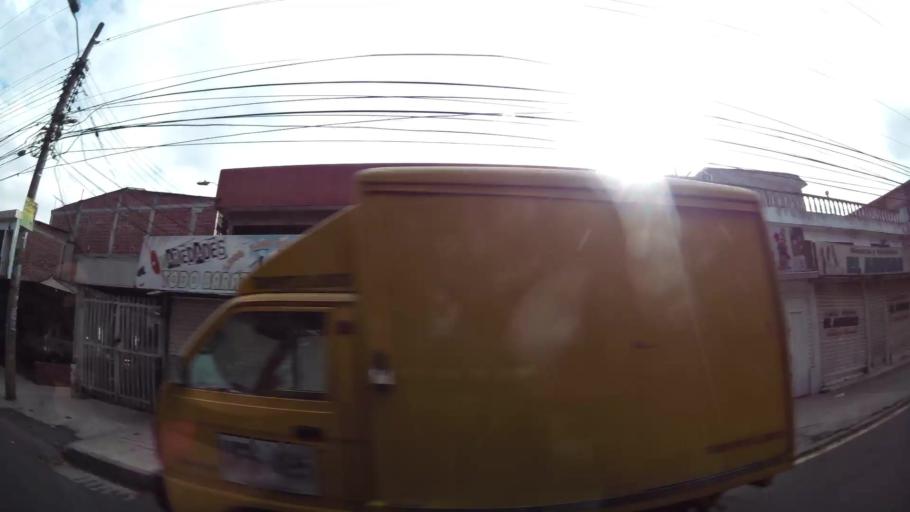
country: CO
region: Valle del Cauca
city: Cali
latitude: 3.4725
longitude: -76.4925
